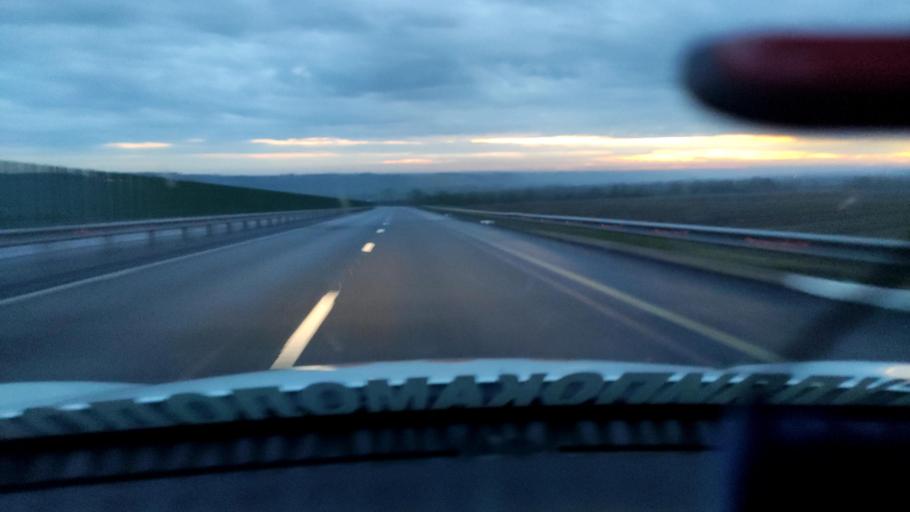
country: RU
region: Rostov
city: Tarasovskiy
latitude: 48.7166
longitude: 40.4021
